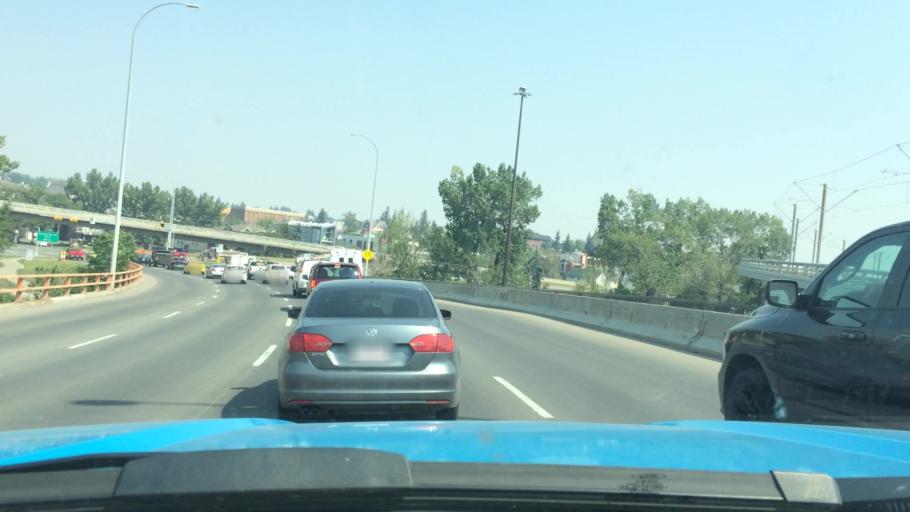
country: CA
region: Alberta
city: Calgary
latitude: 51.0492
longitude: -114.0513
